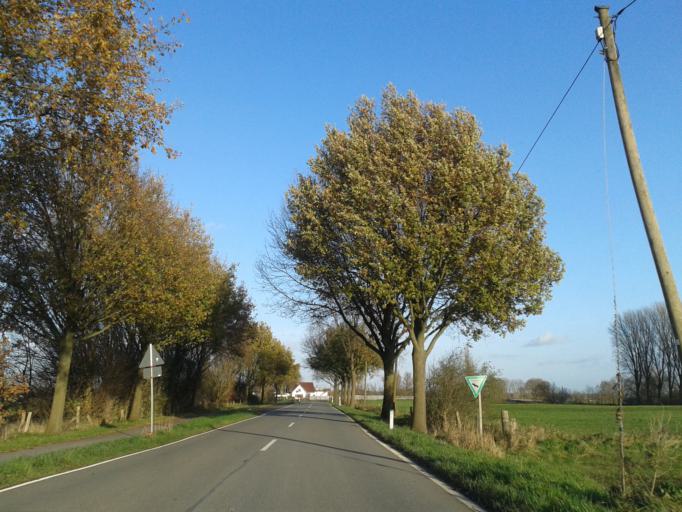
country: DE
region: North Rhine-Westphalia
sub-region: Regierungsbezirk Dusseldorf
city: Xanten
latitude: 51.6625
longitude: 6.4773
